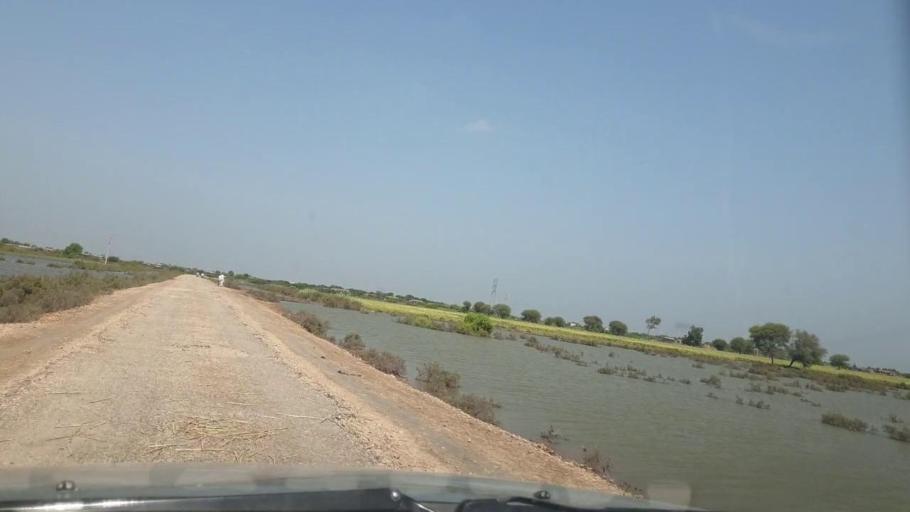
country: PK
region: Sindh
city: Tando Ghulam Ali
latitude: 25.0666
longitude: 68.8011
